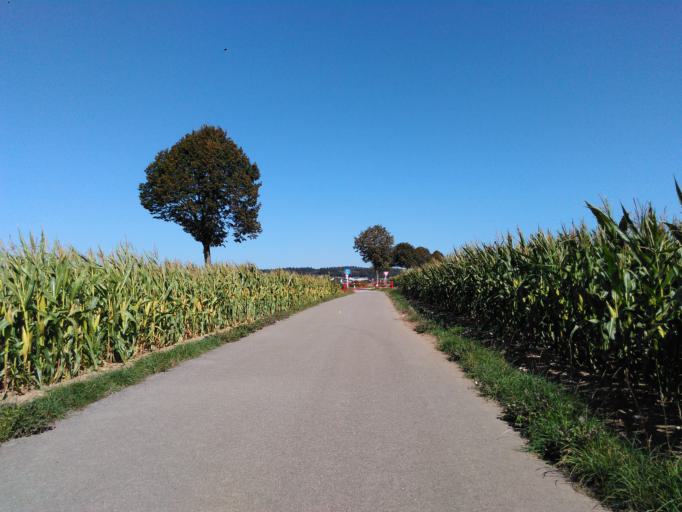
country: LU
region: Diekirch
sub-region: Canton de Redange
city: Rambrouch
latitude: 49.8177
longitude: 5.8364
